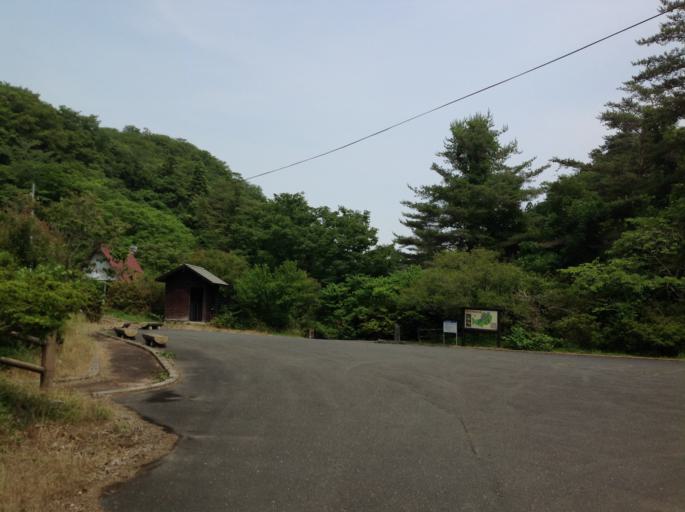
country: JP
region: Iwate
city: Ichinoseki
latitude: 38.8539
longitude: 141.2330
